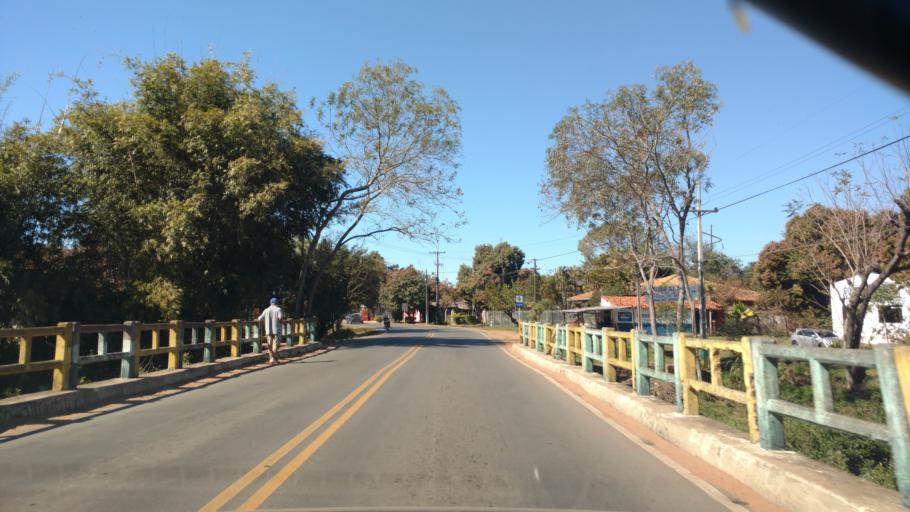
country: PY
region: Paraguari
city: Pirayu
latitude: -25.4576
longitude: -57.2704
